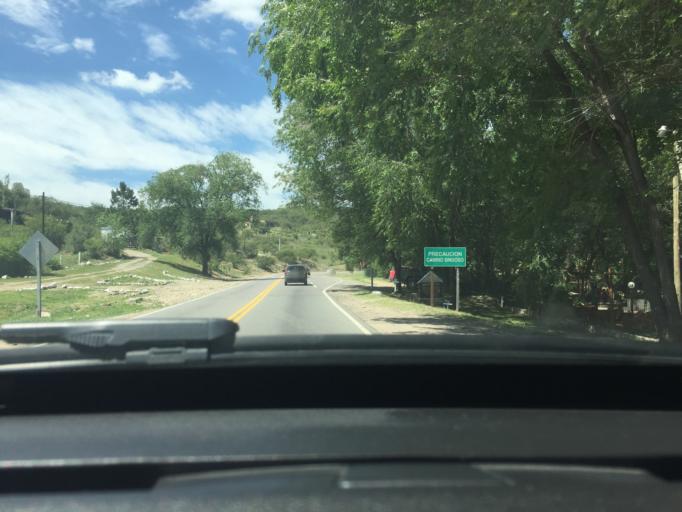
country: AR
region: Cordoba
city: Alta Gracia
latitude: -31.7383
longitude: -64.4529
